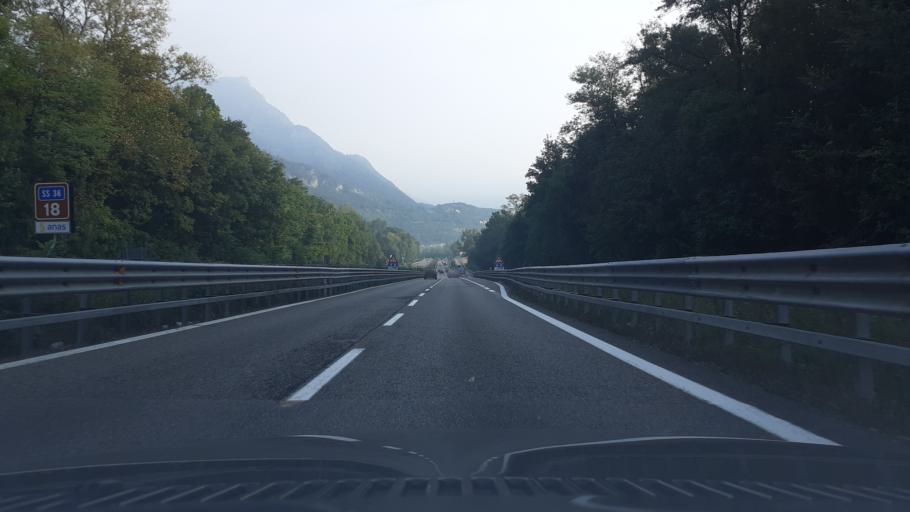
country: IT
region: Lombardy
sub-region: Provincia di Lecco
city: Suello
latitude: 45.8086
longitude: 9.3150
